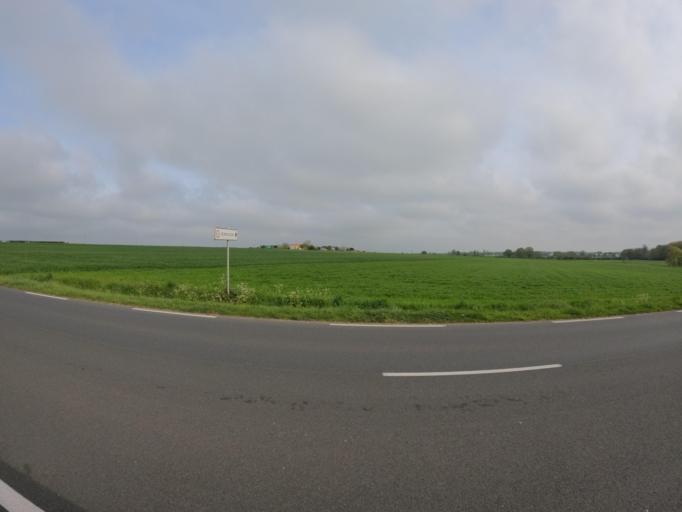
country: FR
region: Pays de la Loire
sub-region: Departement de Maine-et-Loire
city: Vihiers
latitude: 47.1487
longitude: -0.4916
